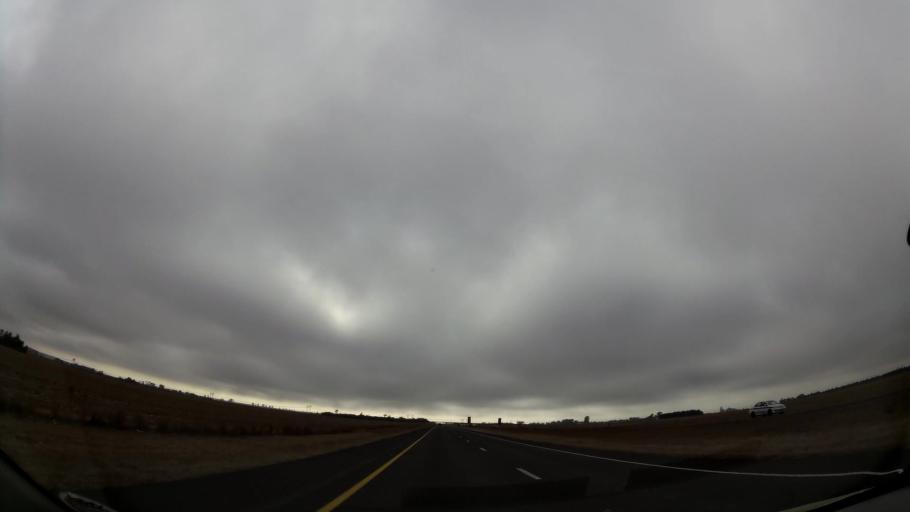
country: ZA
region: Mpumalanga
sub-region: Nkangala District Municipality
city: Delmas
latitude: -26.0622
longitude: 28.7981
